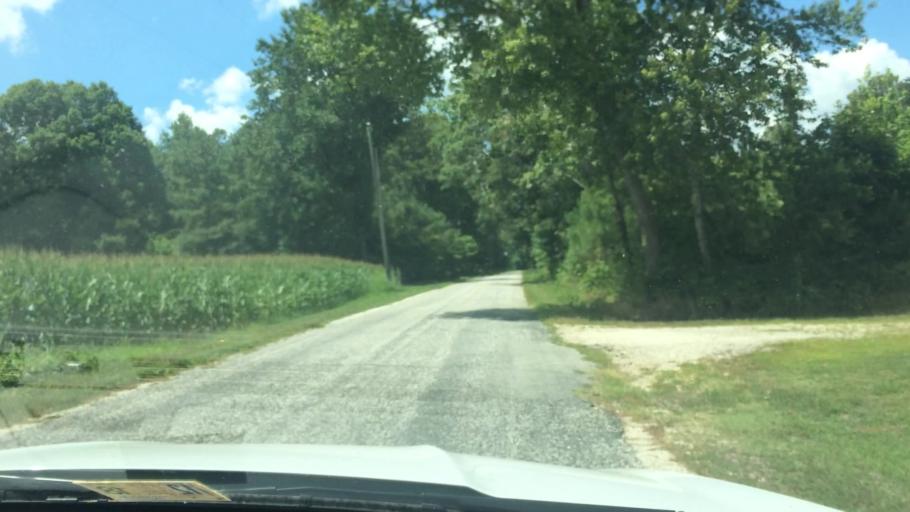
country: US
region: Virginia
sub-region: King William County
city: West Point
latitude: 37.6034
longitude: -76.7849
